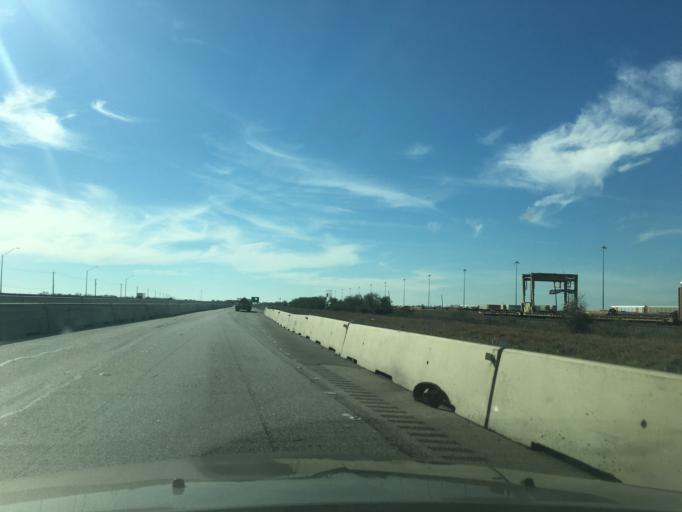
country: US
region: Texas
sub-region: Wharton County
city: East Bernard
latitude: 29.4644
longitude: -95.9722
